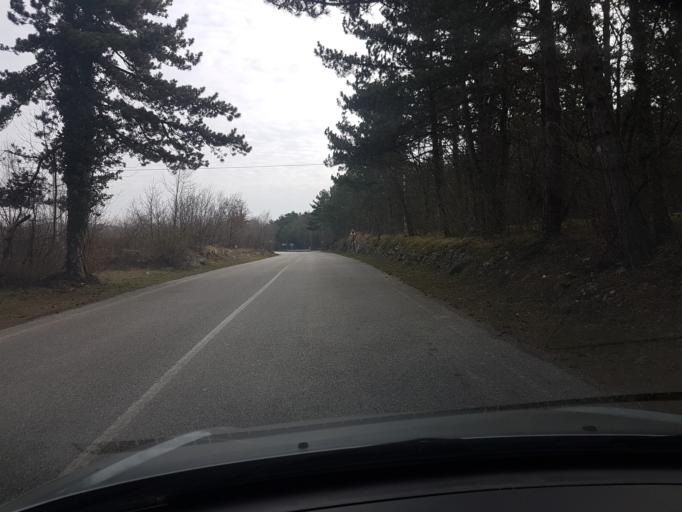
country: IT
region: Friuli Venezia Giulia
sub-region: Provincia di Trieste
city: Aurisina
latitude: 45.7658
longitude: 13.6976
